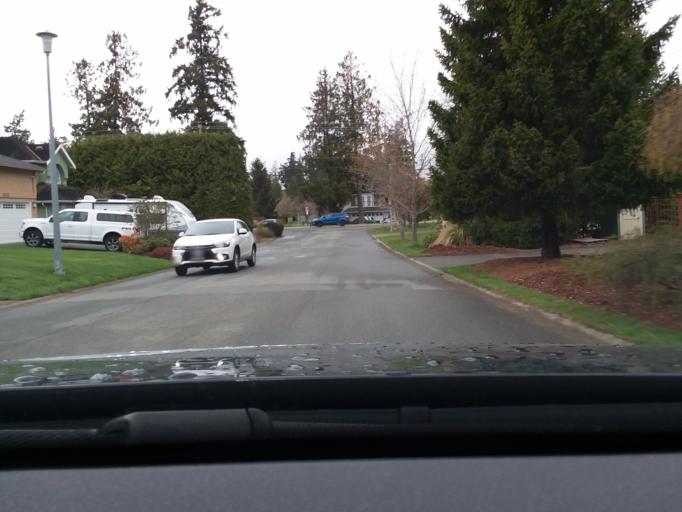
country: CA
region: British Columbia
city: Victoria
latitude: 48.5136
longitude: -123.3778
